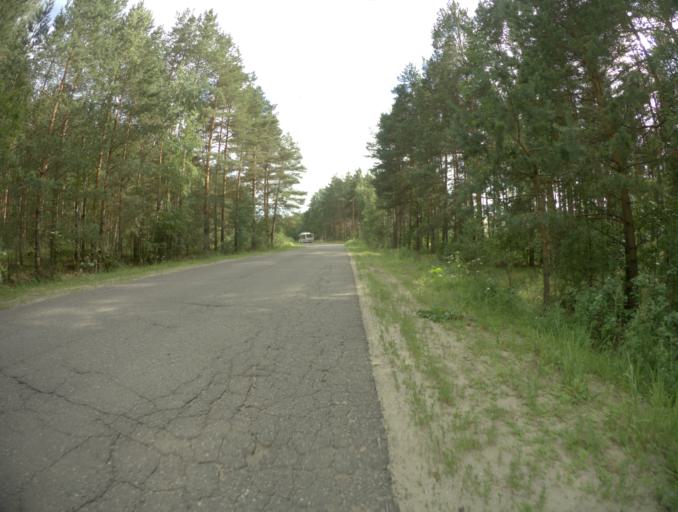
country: RU
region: Vladimir
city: Kommunar
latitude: 56.1379
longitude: 40.4910
